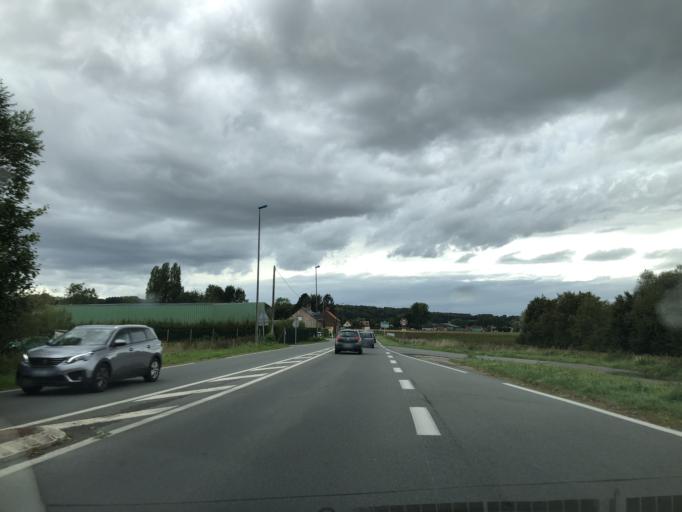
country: FR
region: Picardie
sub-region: Departement de la Somme
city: Abbeville
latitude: 50.1088
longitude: 1.7842
